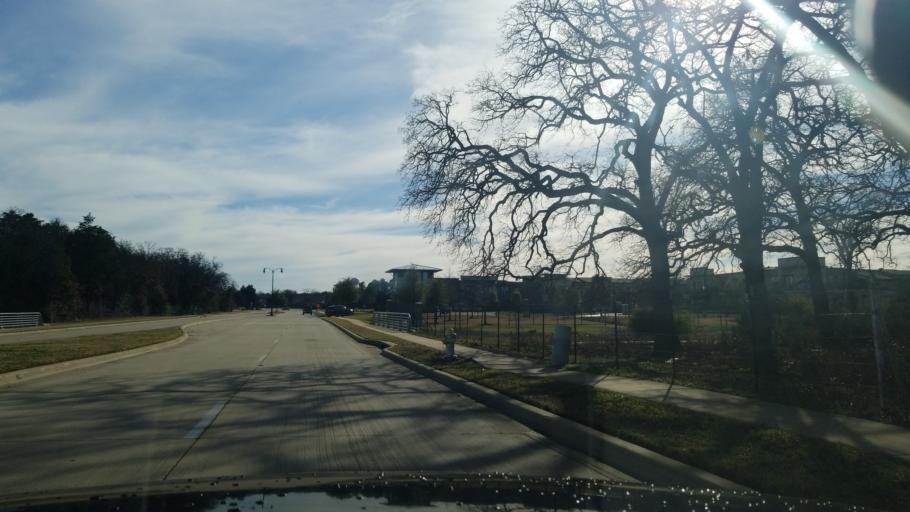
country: US
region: Texas
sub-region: Denton County
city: Corinth
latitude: 33.1473
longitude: -97.0617
